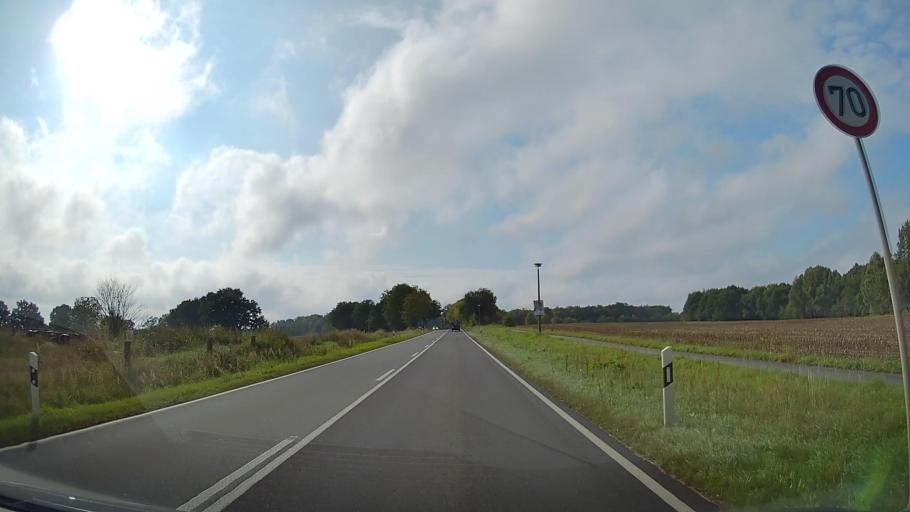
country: DE
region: Mecklenburg-Vorpommern
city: Hagenow
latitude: 53.4356
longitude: 11.1674
